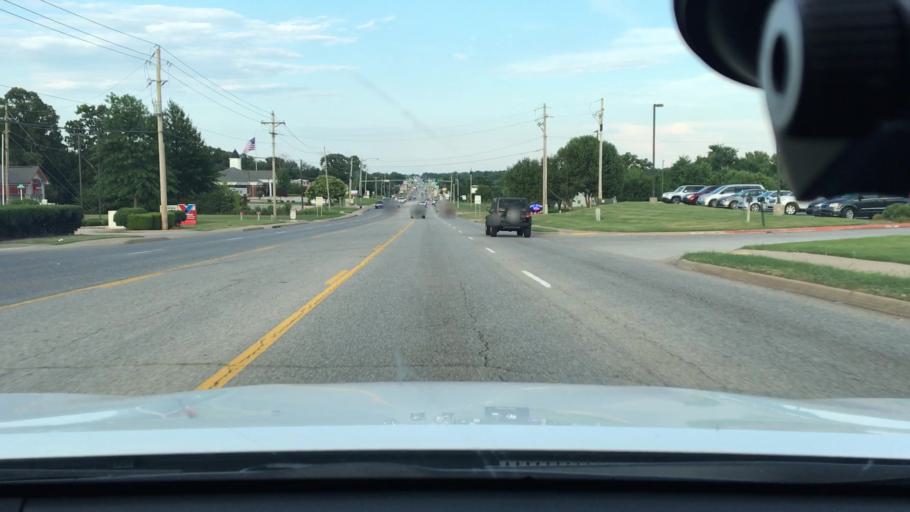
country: US
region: Arkansas
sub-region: Benton County
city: Rogers
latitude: 36.3346
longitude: -94.1690
